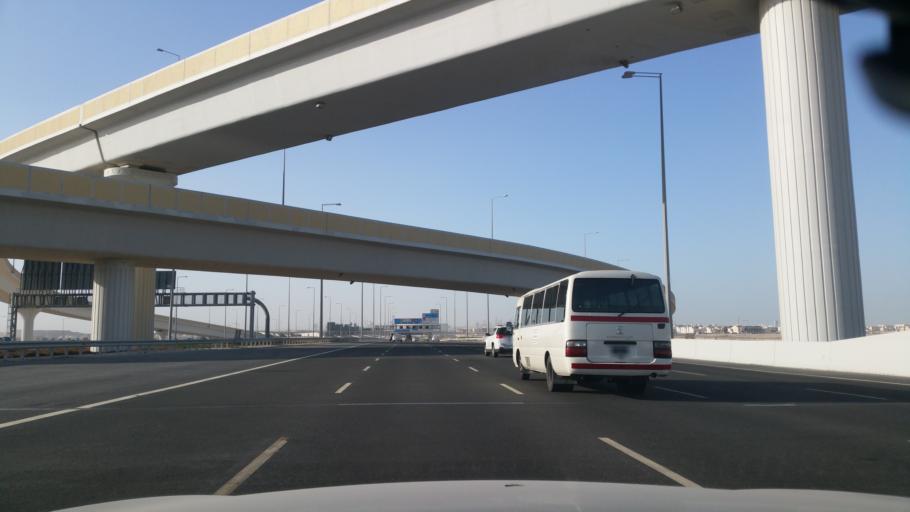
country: QA
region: Al Wakrah
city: Al Wukayr
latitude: 25.2049
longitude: 51.5411
